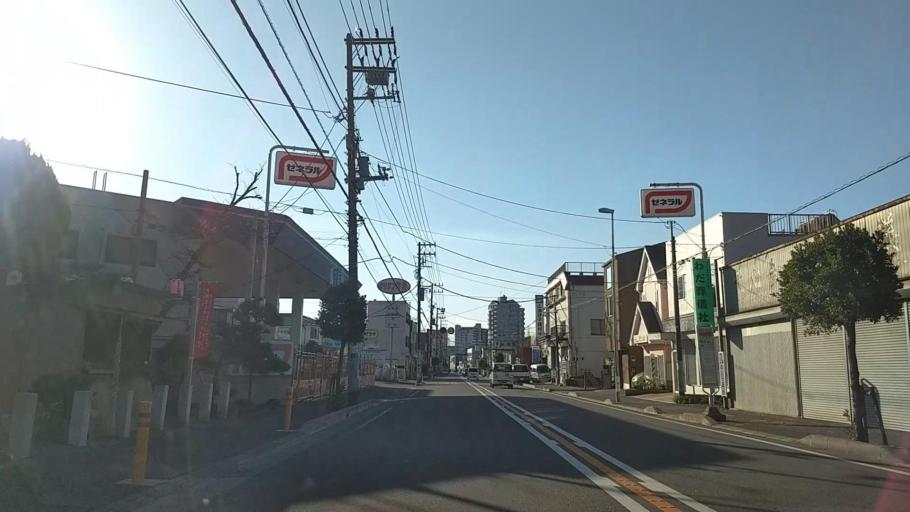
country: JP
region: Kanagawa
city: Fujisawa
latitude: 35.3167
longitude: 139.4858
